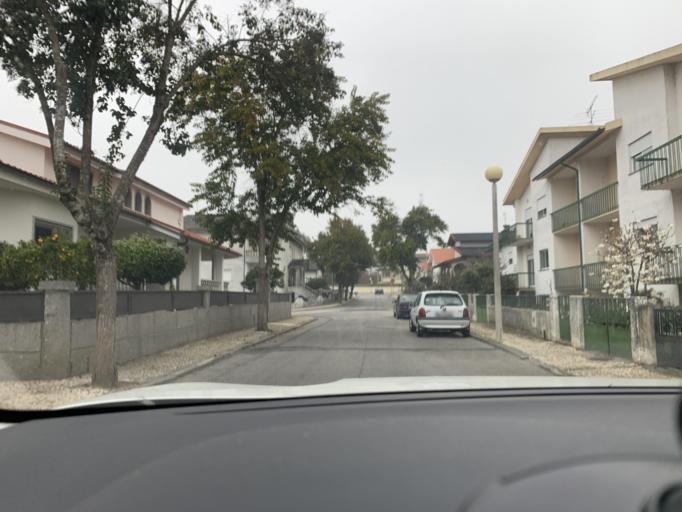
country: PT
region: Viseu
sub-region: Viseu
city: Rio de Loba
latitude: 40.6625
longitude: -7.8889
